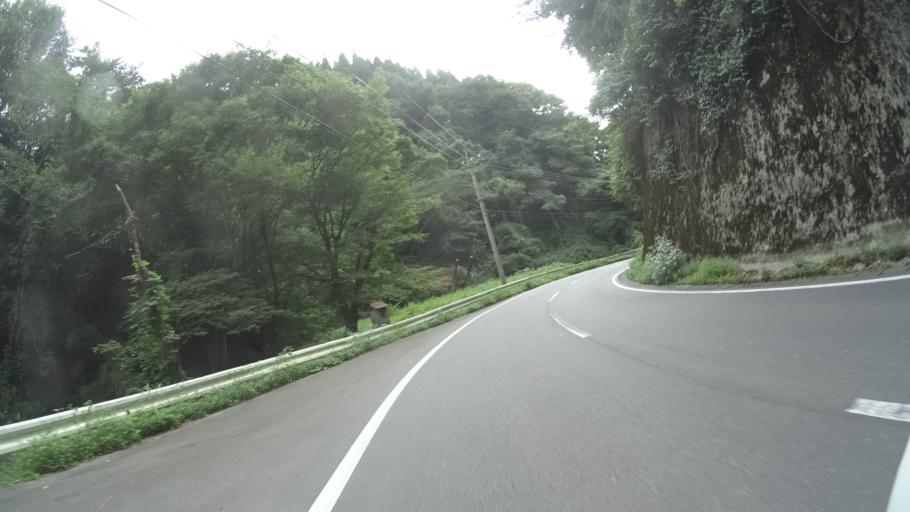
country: JP
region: Kumamoto
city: Aso
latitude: 32.7094
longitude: 131.1326
